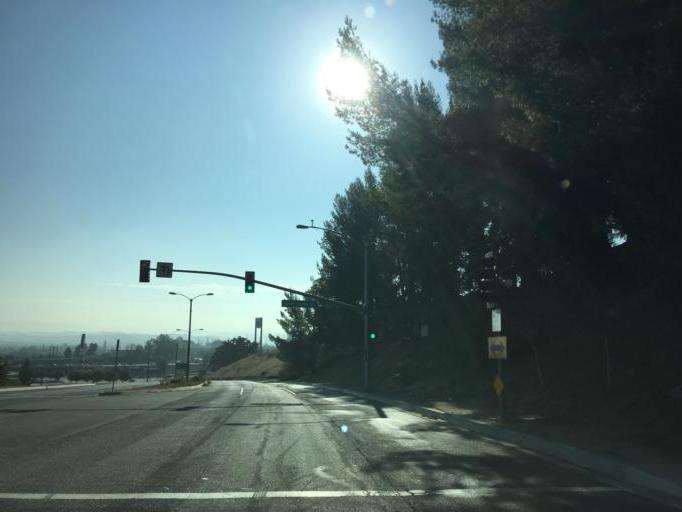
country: US
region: California
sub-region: Los Angeles County
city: Valencia
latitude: 34.4204
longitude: -118.5883
